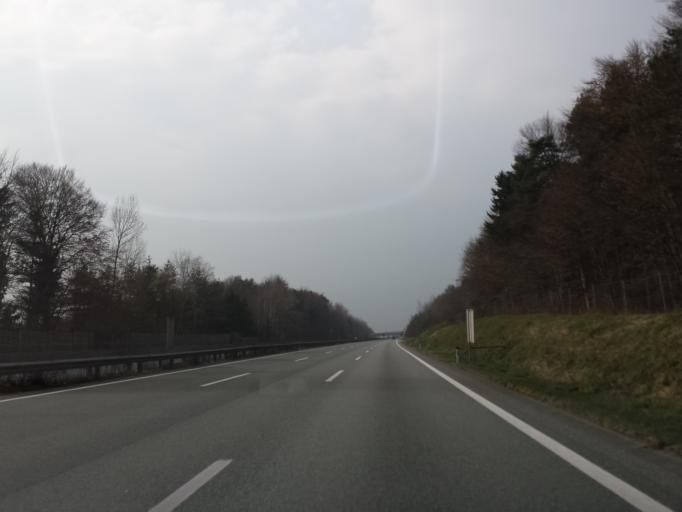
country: AT
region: Styria
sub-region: Politischer Bezirk Weiz
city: Sinabelkirchen
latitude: 47.1018
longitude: 15.7849
